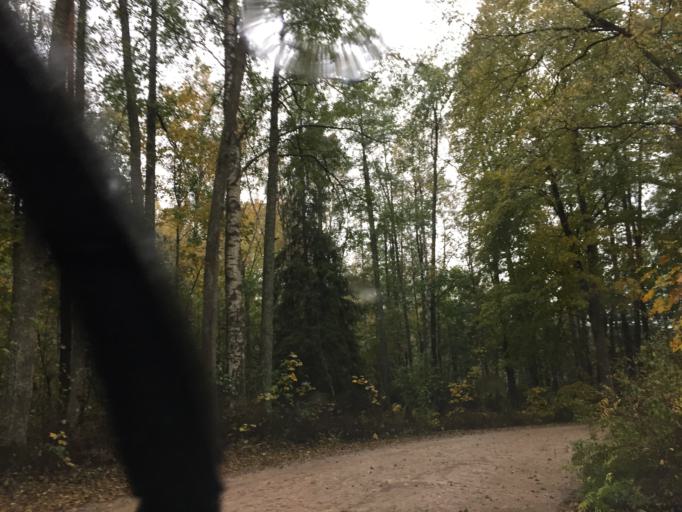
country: LV
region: Engure
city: Smarde
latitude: 56.9176
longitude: 23.4683
